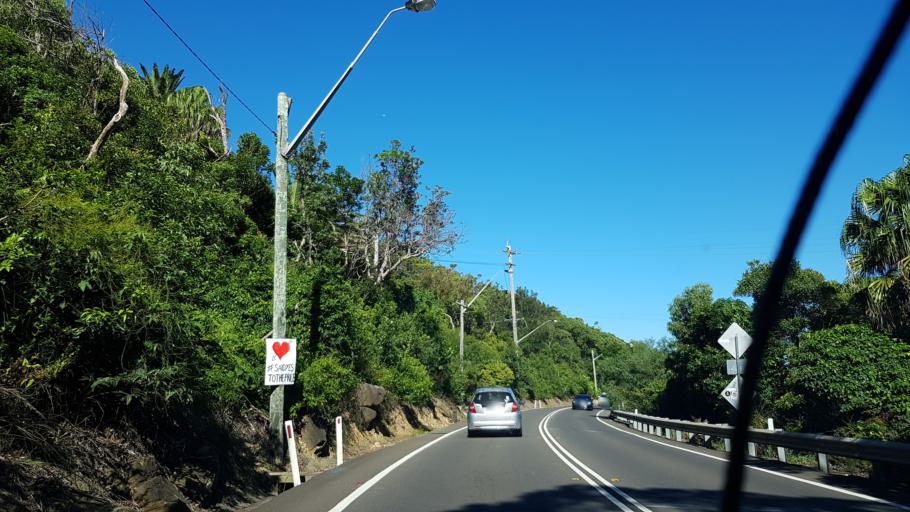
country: AU
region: New South Wales
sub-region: Pittwater
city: Bilgola Beach
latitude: -33.6428
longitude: 151.3236
